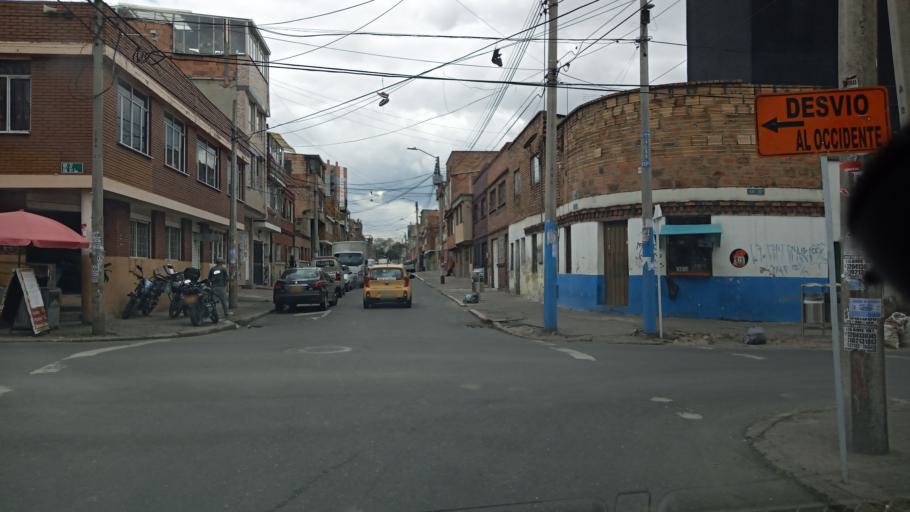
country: CO
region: Bogota D.C.
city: Bogota
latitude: 4.5862
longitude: -74.1152
